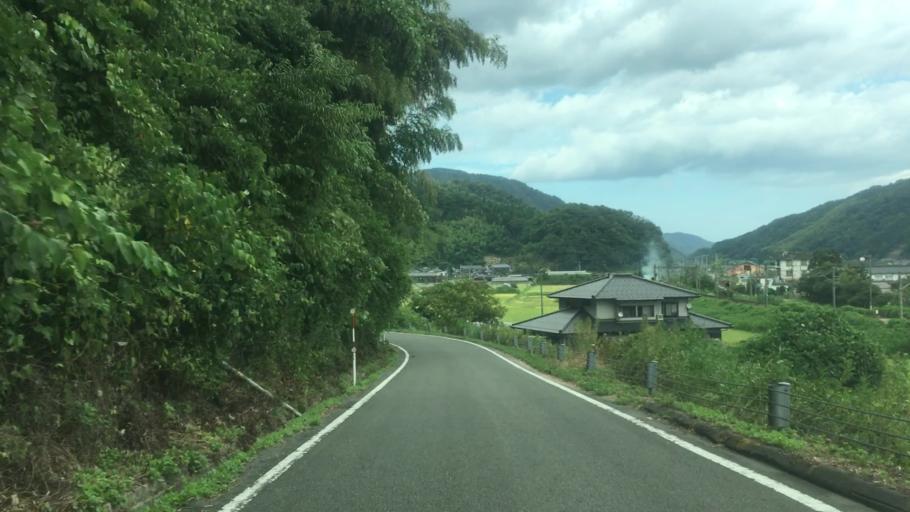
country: JP
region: Hyogo
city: Toyooka
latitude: 35.5884
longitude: 134.7982
